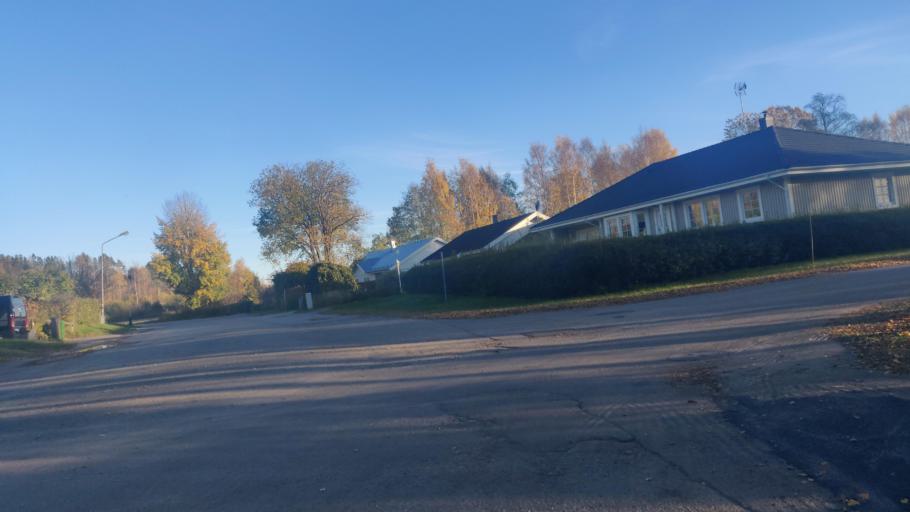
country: SE
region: Vaesternorrland
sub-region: Sundsvalls Kommun
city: Skottsund
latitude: 62.2899
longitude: 17.3921
